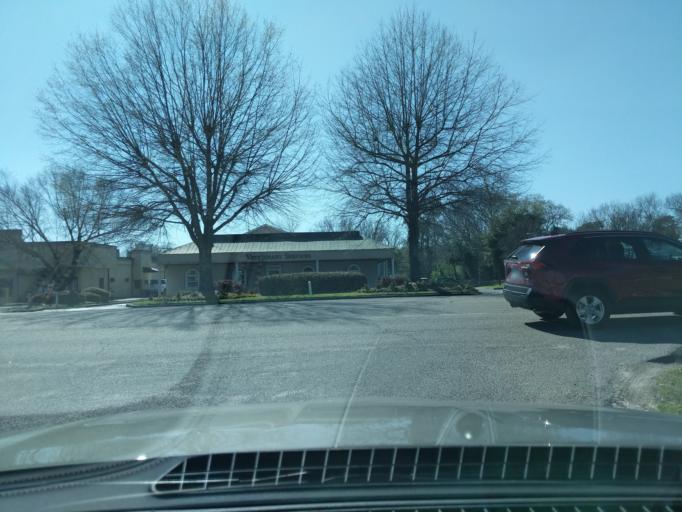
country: US
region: South Carolina
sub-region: Aiken County
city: Aiken
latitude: 33.5275
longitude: -81.7217
